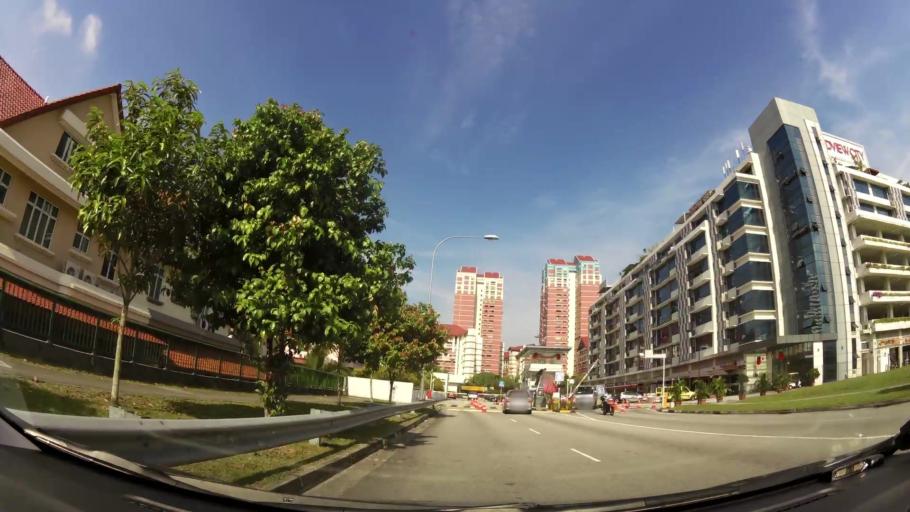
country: SG
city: Singapore
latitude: 1.3573
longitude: 103.8340
